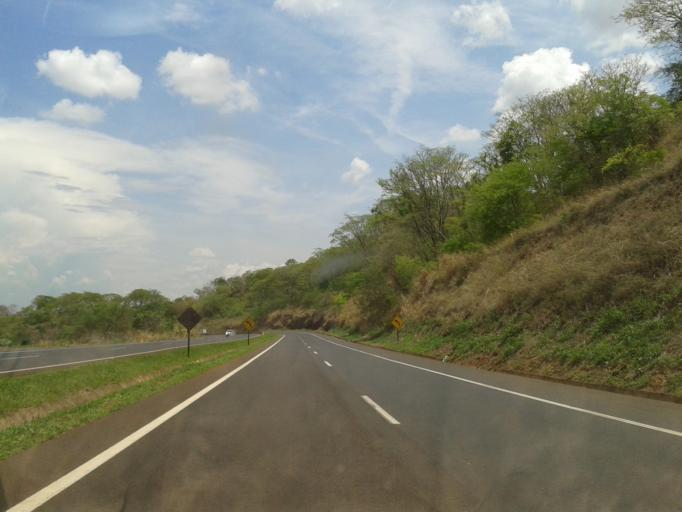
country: BR
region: Minas Gerais
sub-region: Araguari
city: Araguari
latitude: -18.7309
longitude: -48.2137
